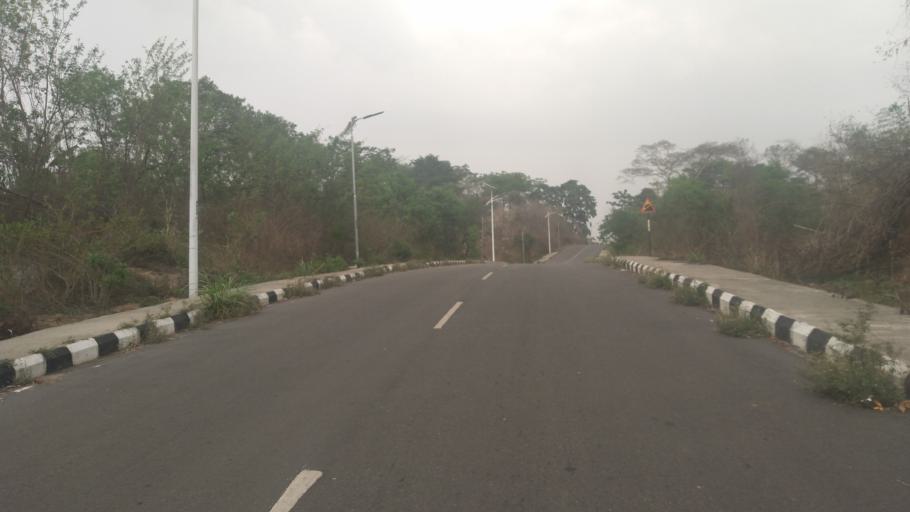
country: NG
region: Ondo
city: Ilare
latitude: 7.2963
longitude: 5.1393
